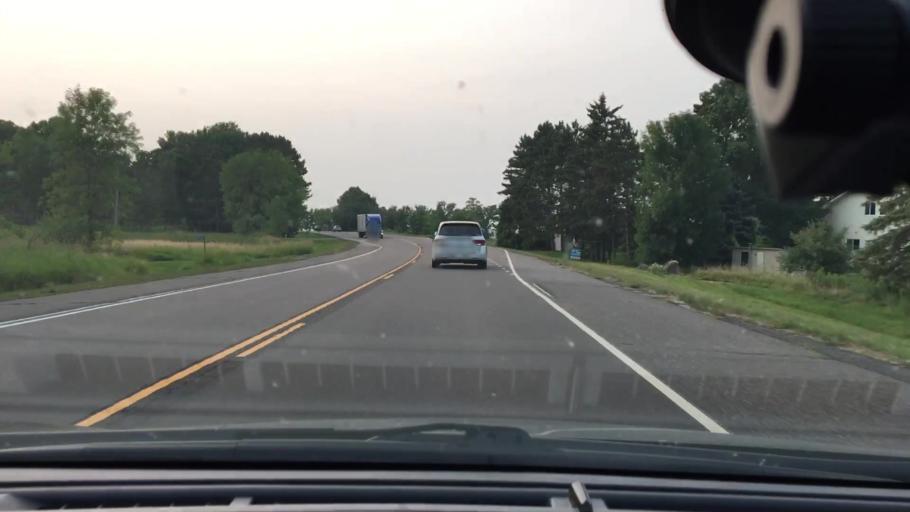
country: US
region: Minnesota
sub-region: Mille Lacs County
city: Vineland
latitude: 46.1333
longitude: -93.6905
